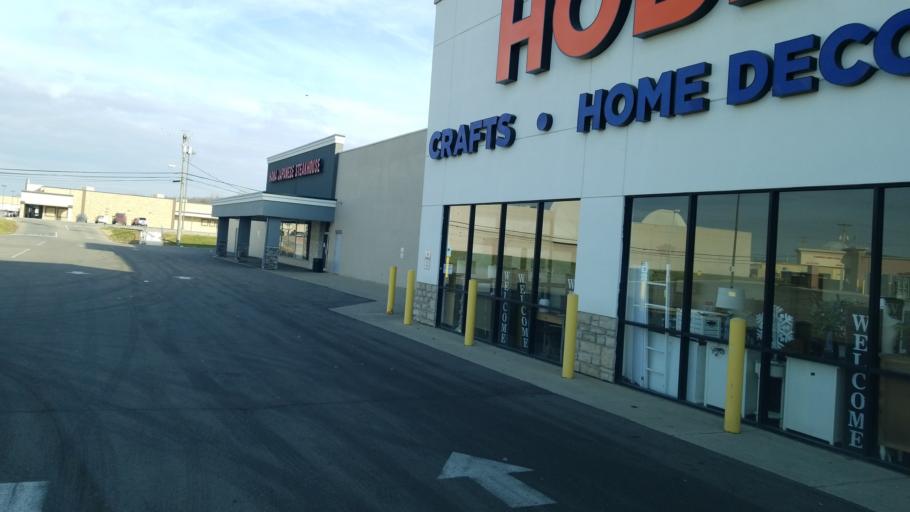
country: US
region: Ohio
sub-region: Ross County
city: Chillicothe
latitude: 39.3554
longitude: -82.9743
